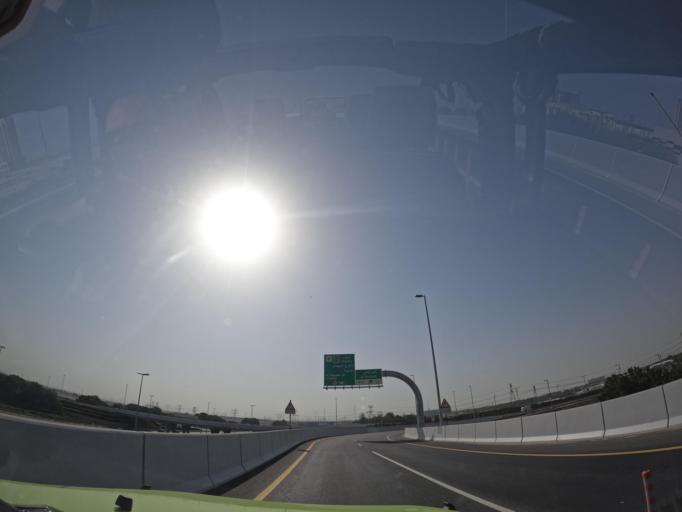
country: AE
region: Dubai
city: Dubai
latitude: 25.1756
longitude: 55.3195
